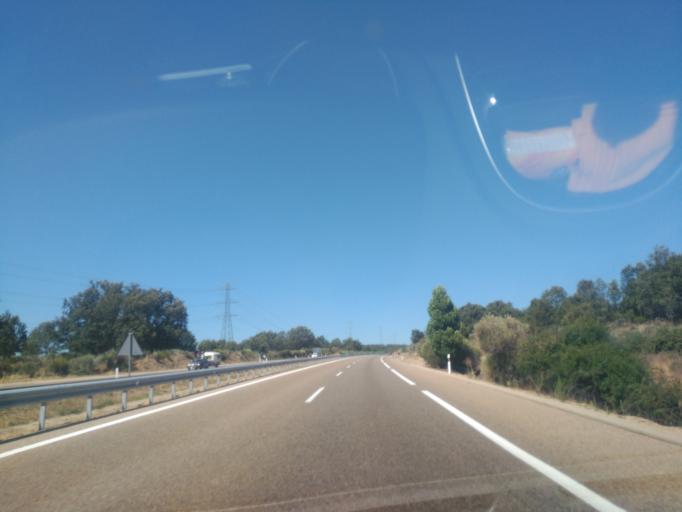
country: ES
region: Castille and Leon
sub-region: Provincia de Zamora
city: Mombuey
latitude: 42.0176
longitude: -6.3354
